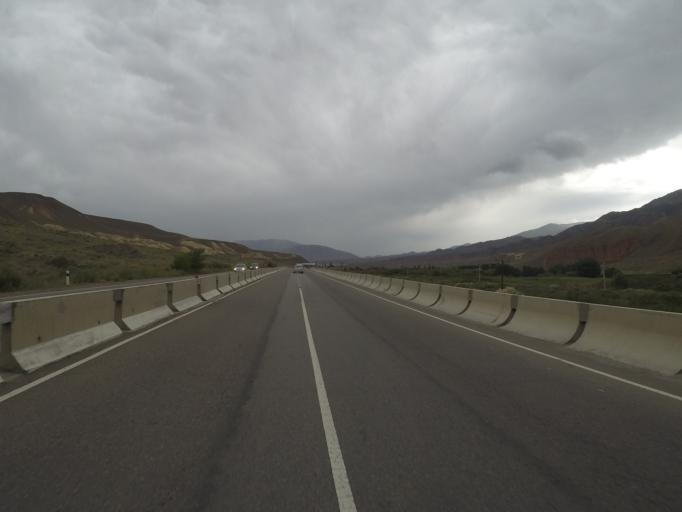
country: KG
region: Chuy
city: Bystrovka
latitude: 42.5442
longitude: 75.8142
